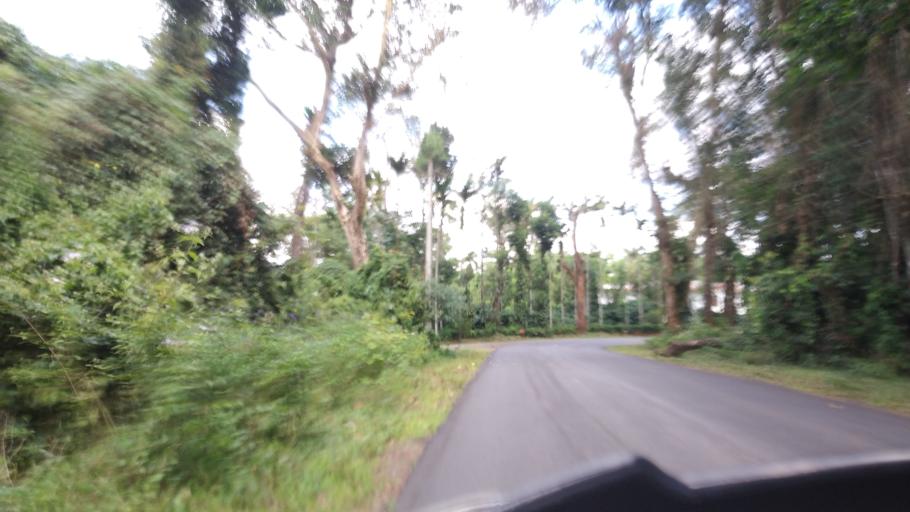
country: IN
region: Karnataka
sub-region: Kodagu
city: Ponnampet
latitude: 12.0336
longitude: 75.9265
